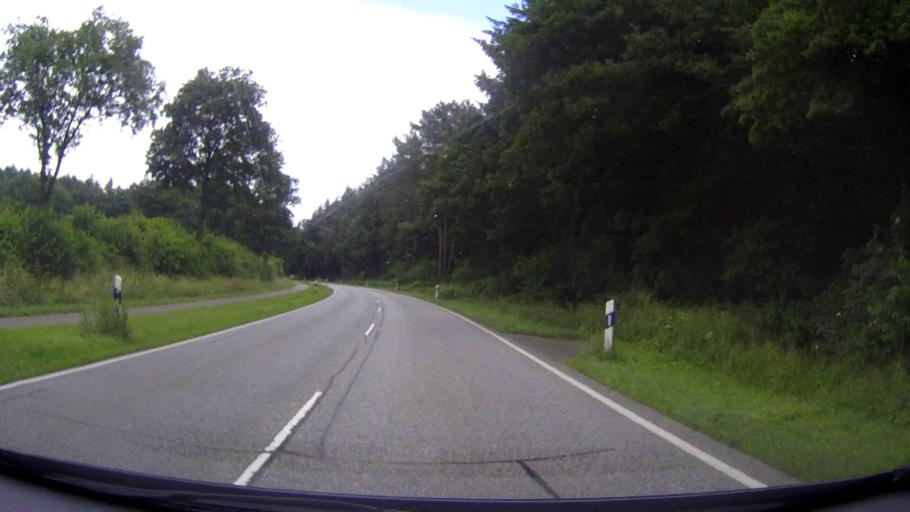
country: DE
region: Schleswig-Holstein
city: Aukrug
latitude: 54.0666
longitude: 9.7580
